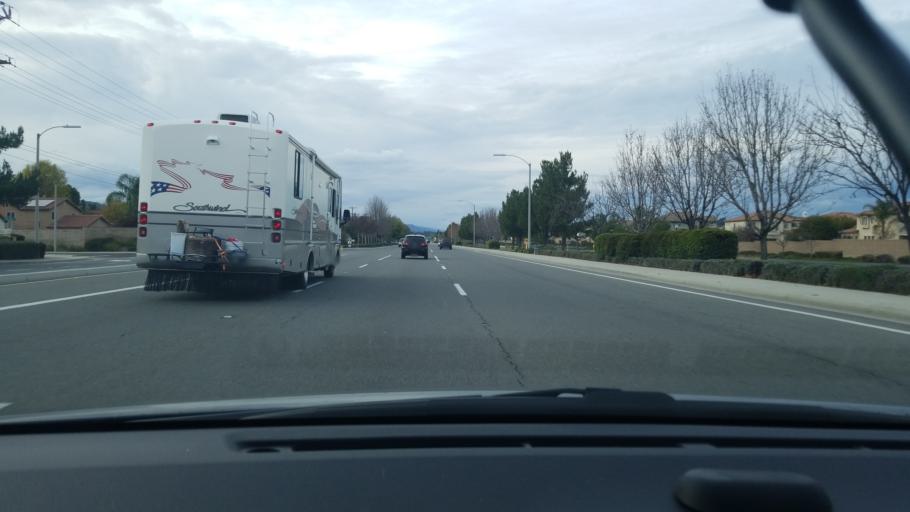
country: US
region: California
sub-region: Riverside County
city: Temecula
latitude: 33.4629
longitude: -117.1120
